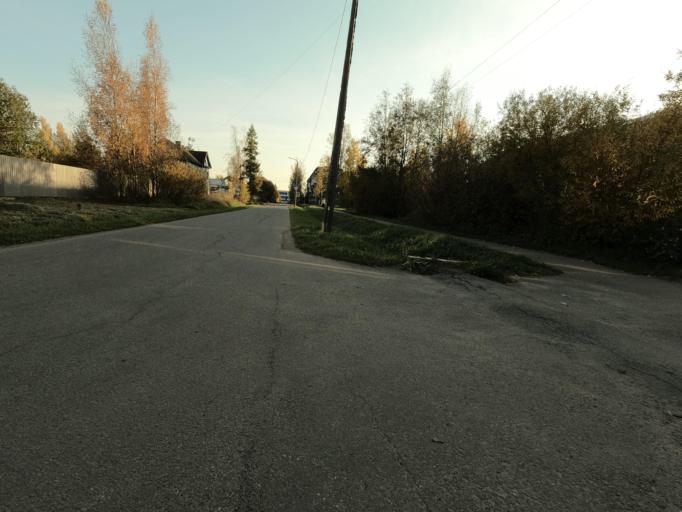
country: RU
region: Leningrad
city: Mga
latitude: 59.7582
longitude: 31.0690
